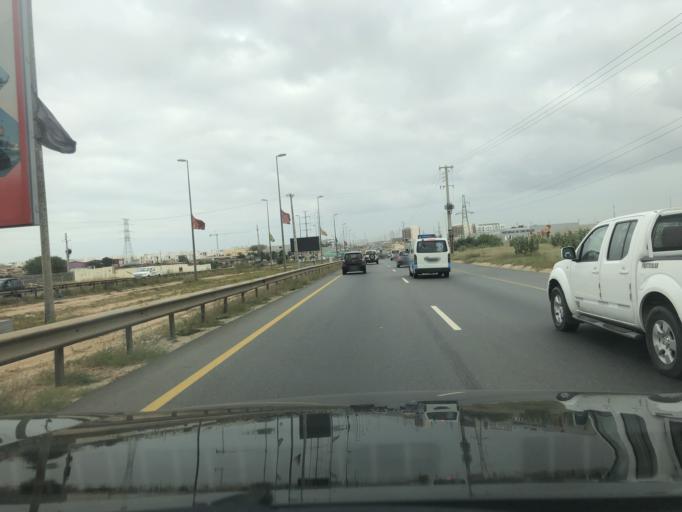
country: AO
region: Luanda
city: Luanda
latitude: -8.9738
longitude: 13.2255
